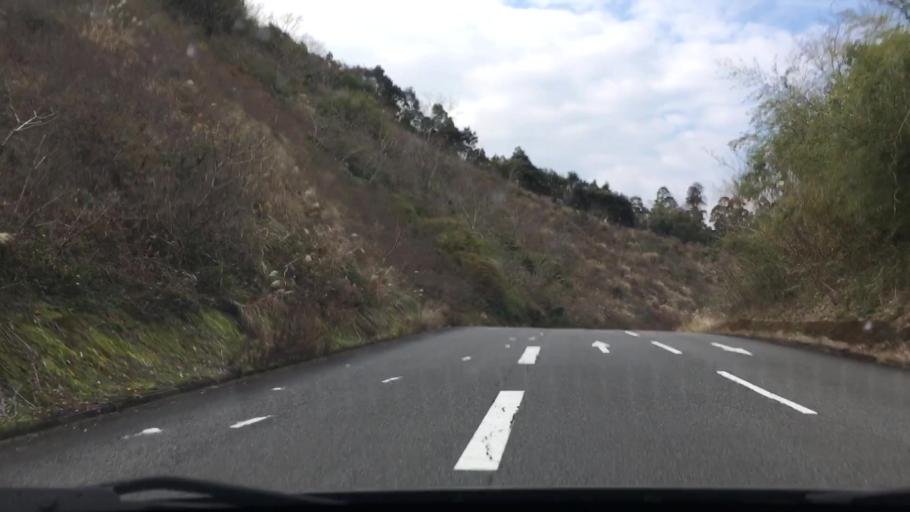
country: JP
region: Miyazaki
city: Nichinan
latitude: 31.6378
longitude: 131.3344
